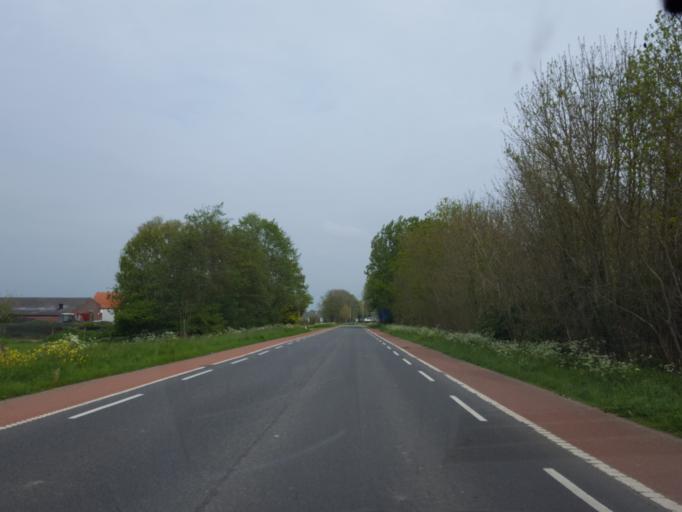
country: NL
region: Gelderland
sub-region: Gemeente Wijchen
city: Bergharen
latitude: 51.8820
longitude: 5.6560
